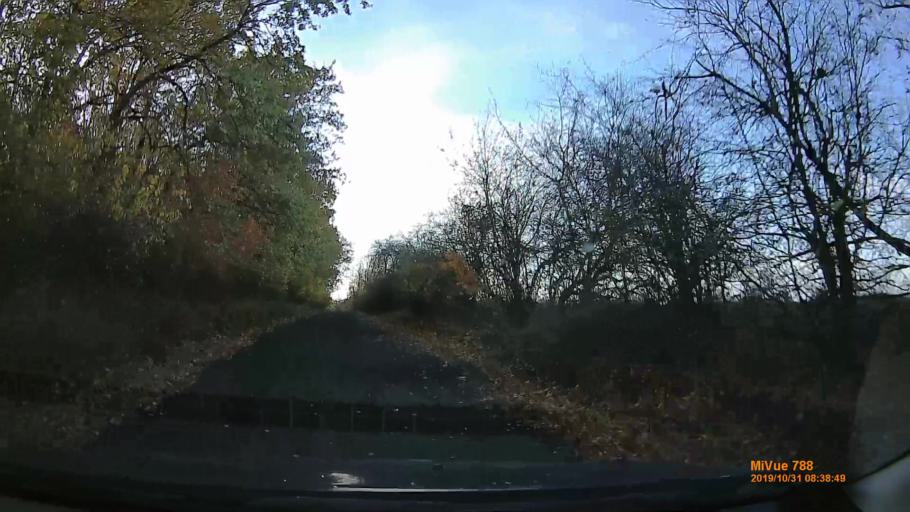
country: HU
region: Pest
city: Pand
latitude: 47.3151
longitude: 19.6496
